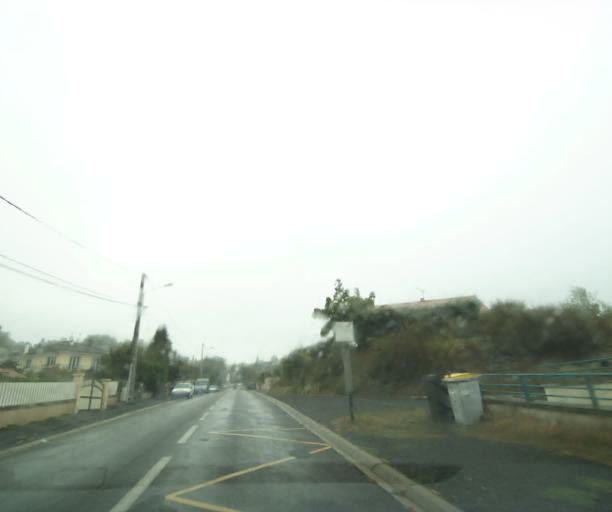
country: FR
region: Auvergne
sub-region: Departement du Puy-de-Dome
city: Chateaugay
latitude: 45.8451
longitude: 3.0921
